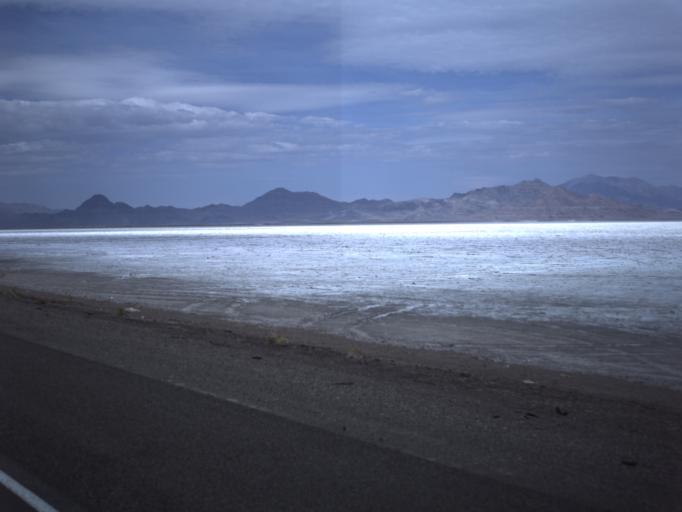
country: US
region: Utah
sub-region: Tooele County
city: Wendover
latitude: 40.7385
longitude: -113.8063
